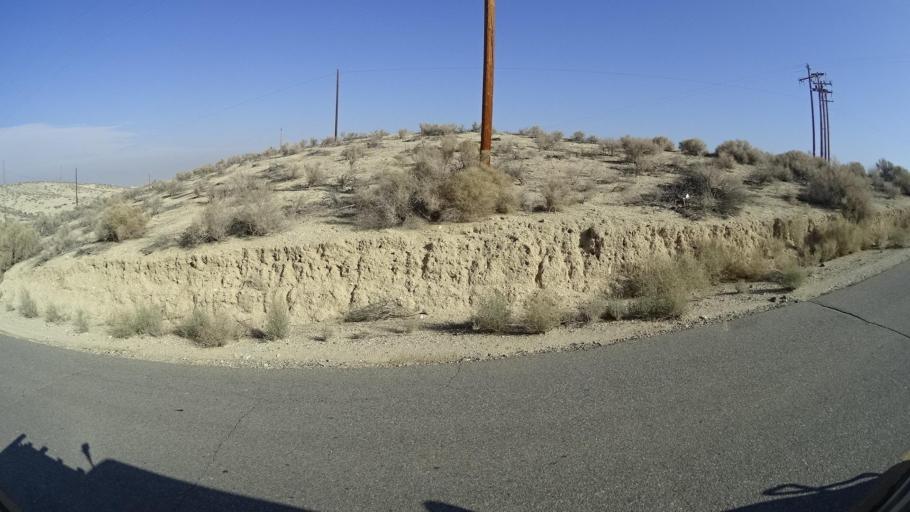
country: US
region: California
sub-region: Kern County
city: Taft Heights
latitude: 35.1448
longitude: -119.5128
